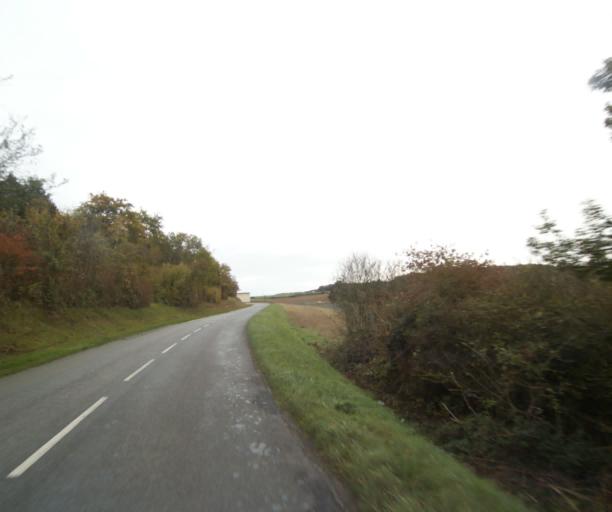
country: FR
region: Centre
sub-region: Departement d'Eure-et-Loir
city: Vert-en-Drouais
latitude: 48.7522
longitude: 1.3114
